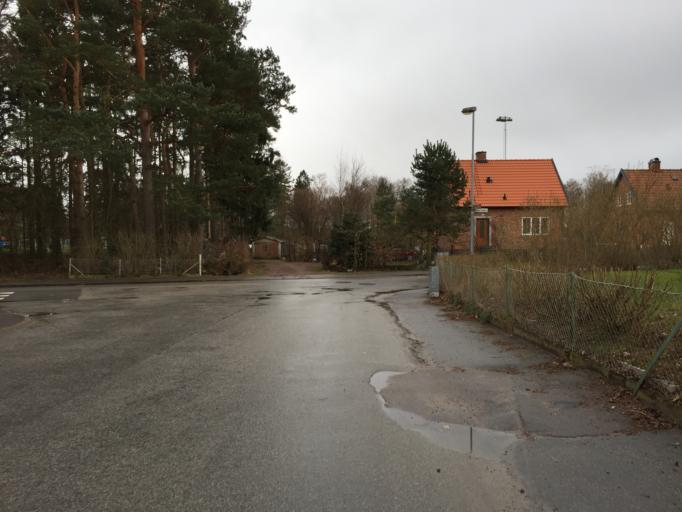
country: SE
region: Skane
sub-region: Lunds Kommun
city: Veberod
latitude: 55.6348
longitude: 13.5006
